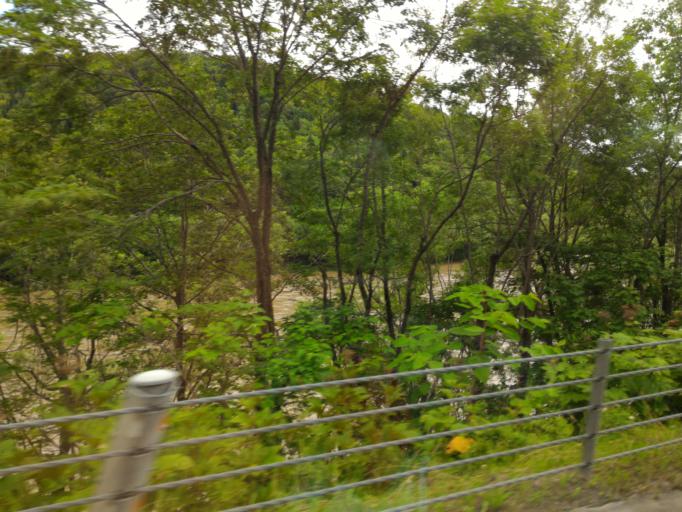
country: JP
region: Hokkaido
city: Nayoro
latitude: 44.7252
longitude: 142.2348
